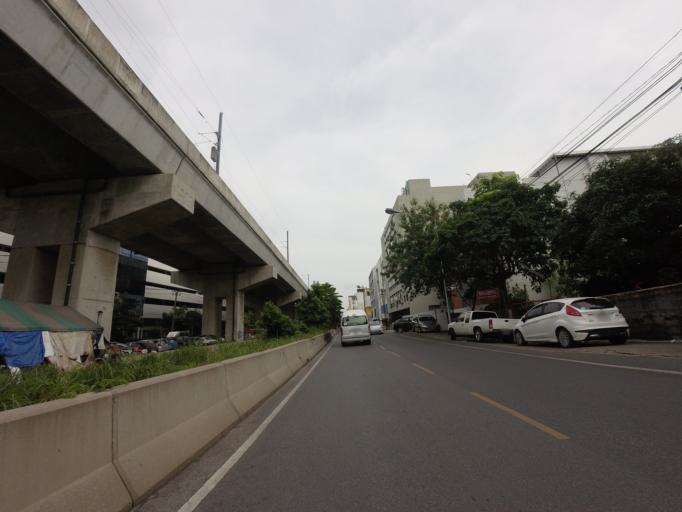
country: TH
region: Bangkok
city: Watthana
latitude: 13.7457
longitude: 100.5836
